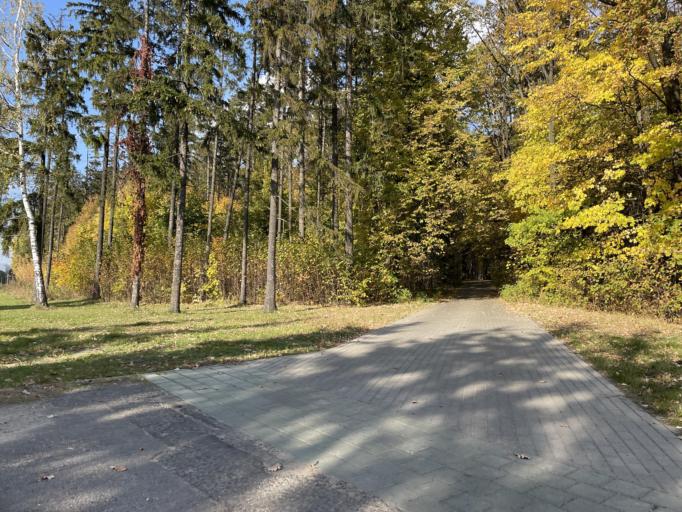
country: BY
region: Minsk
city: Minsk
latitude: 53.9100
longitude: 27.6121
